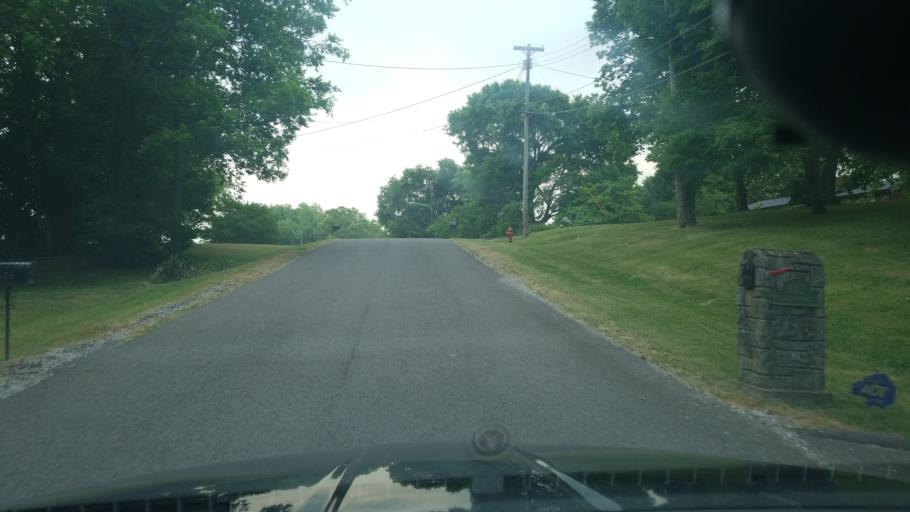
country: US
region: Tennessee
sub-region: Davidson County
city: Goodlettsville
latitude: 36.2595
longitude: -86.7417
